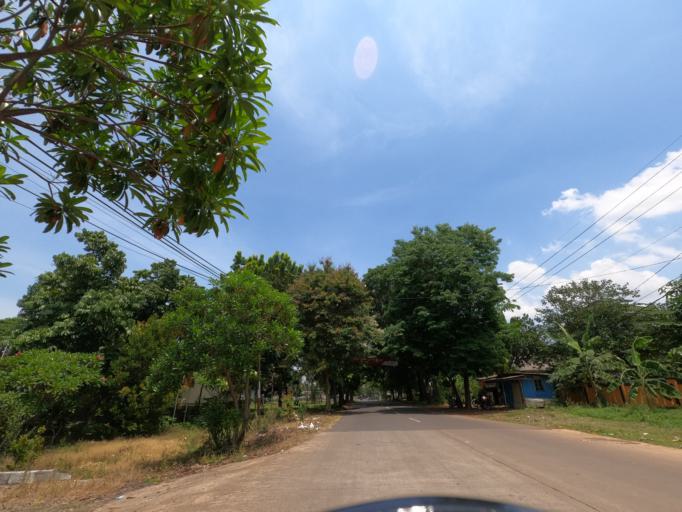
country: ID
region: West Java
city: Pamanukan
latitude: -6.5457
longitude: 107.7666
